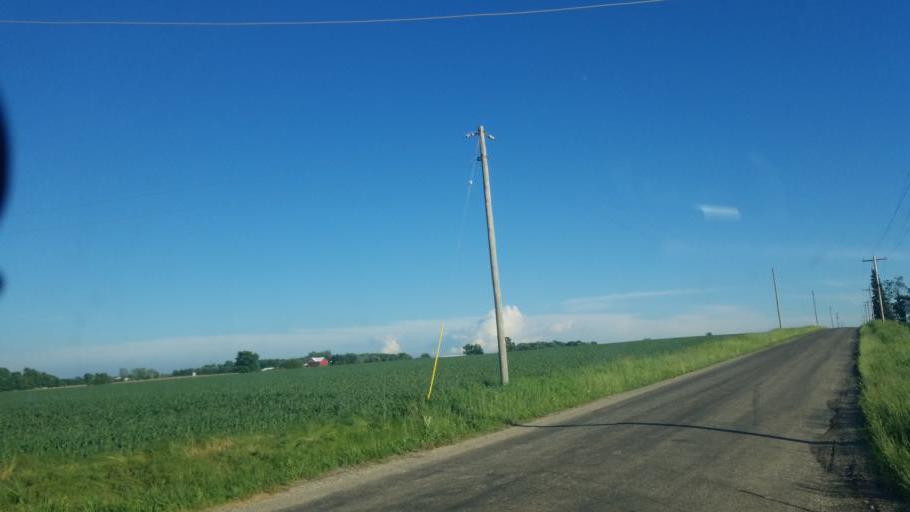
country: US
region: Indiana
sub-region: Marshall County
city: Bremen
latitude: 41.4263
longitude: -86.0830
